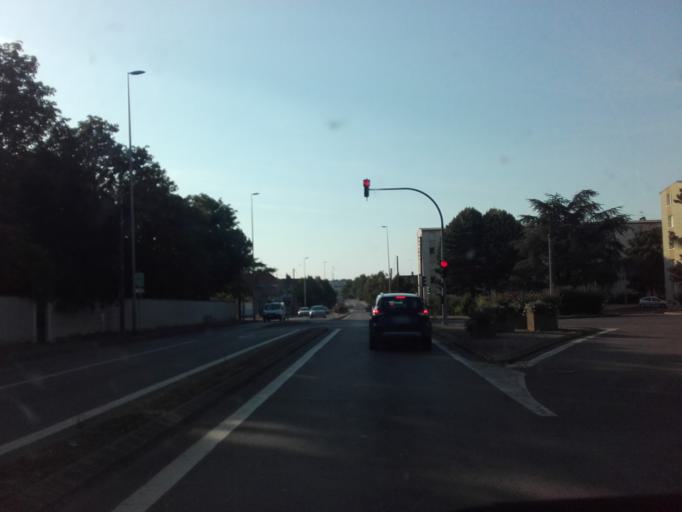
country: FR
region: Bourgogne
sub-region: Departement de l'Yonne
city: Auxerre
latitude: 47.7927
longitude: 3.5879
